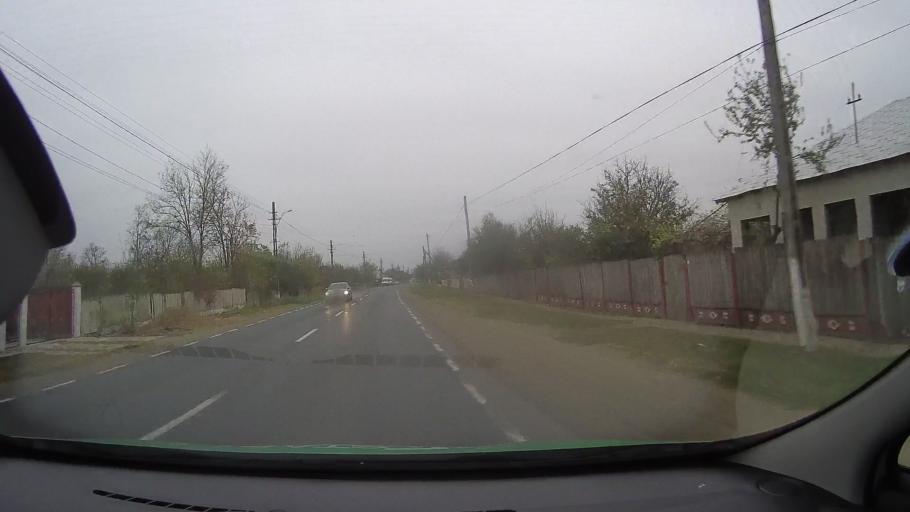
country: RO
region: Braila
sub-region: Comuna Baraganul
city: Baraganul
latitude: 44.8091
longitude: 27.5137
